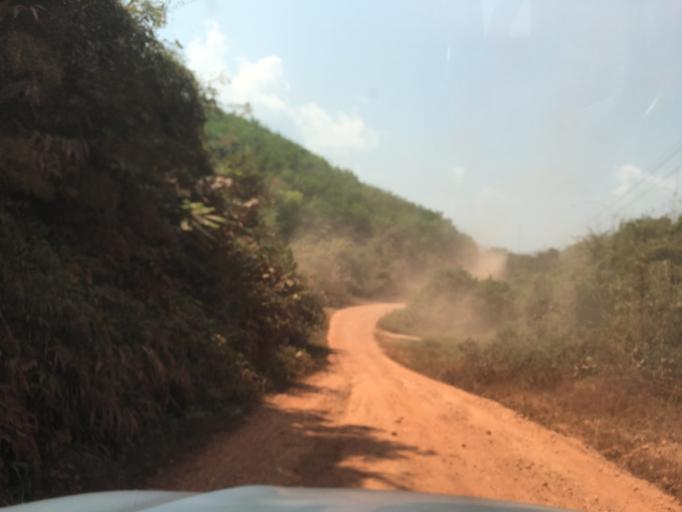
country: LA
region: Bolikhamxai
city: Bolikhan
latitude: 18.7508
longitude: 103.6082
